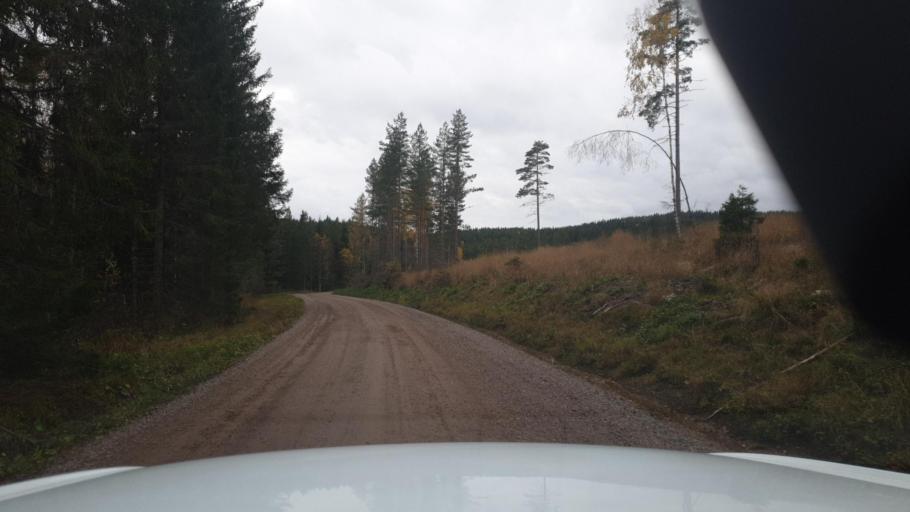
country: SE
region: Vaermland
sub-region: Arvika Kommun
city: Arvika
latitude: 59.9876
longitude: 12.6619
